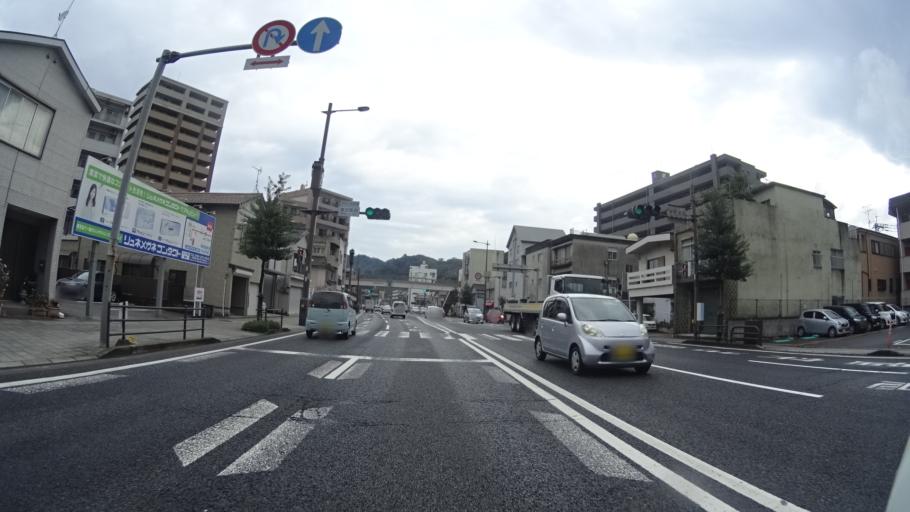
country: JP
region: Kagoshima
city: Kagoshima-shi
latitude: 31.6049
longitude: 130.5655
